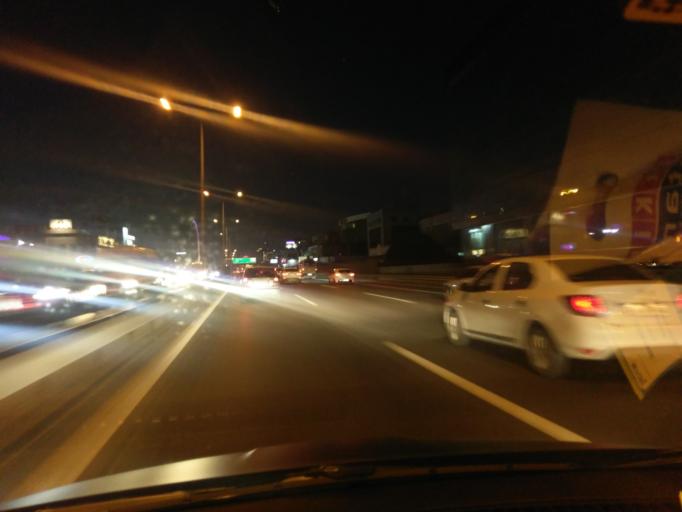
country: TR
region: Istanbul
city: Mahmutbey
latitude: 41.0202
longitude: 28.8121
